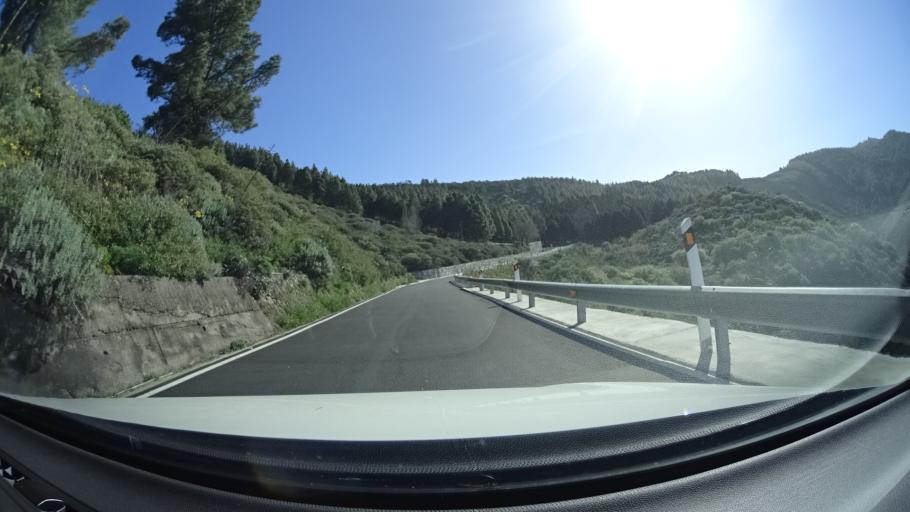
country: ES
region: Canary Islands
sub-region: Provincia de Las Palmas
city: Artenara
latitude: 28.0311
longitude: -15.6239
